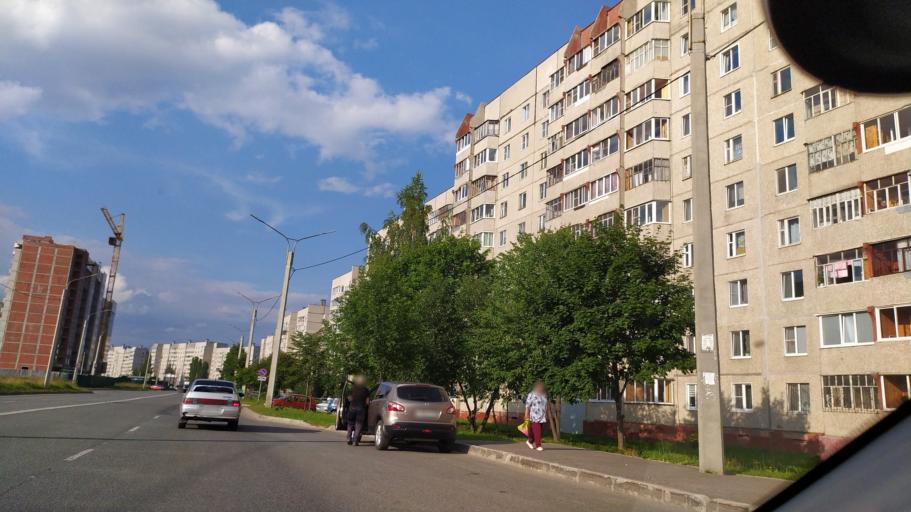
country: RU
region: Chuvashia
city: Novocheboksarsk
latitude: 56.1142
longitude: 47.4408
